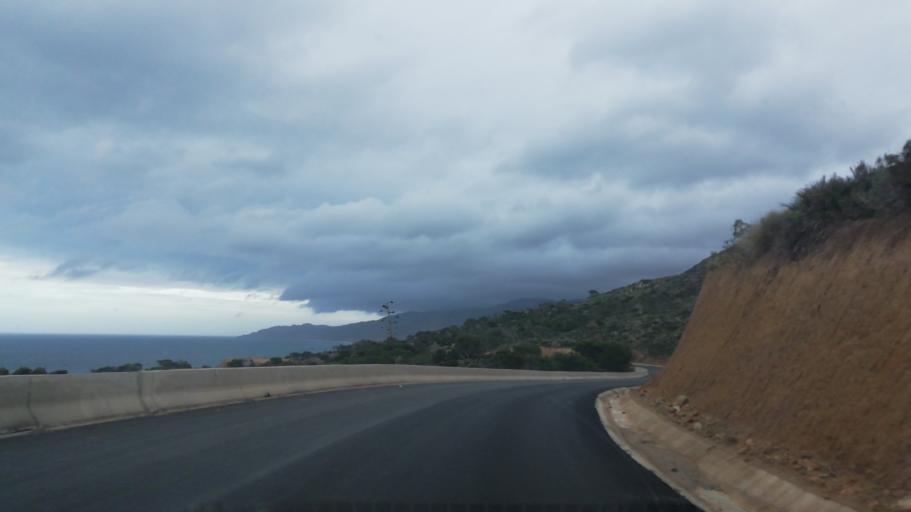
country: DZ
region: Oran
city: Bir el Djir
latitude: 35.7744
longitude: -0.5146
